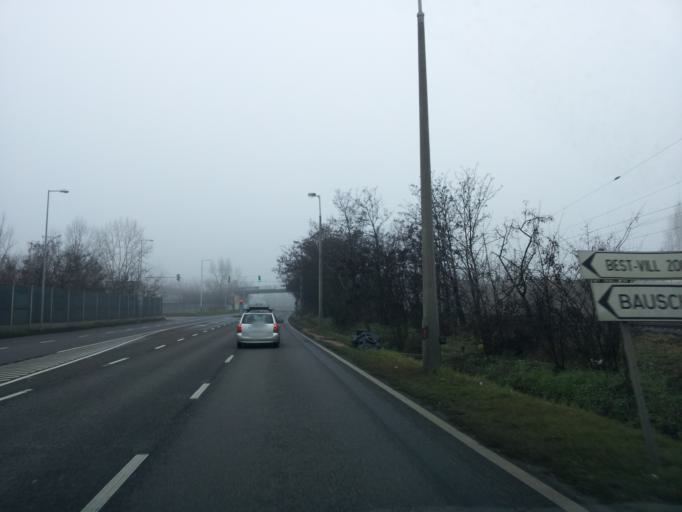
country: HU
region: Budapest
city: Budapest XXII. keruelet
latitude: 47.4100
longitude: 19.0321
